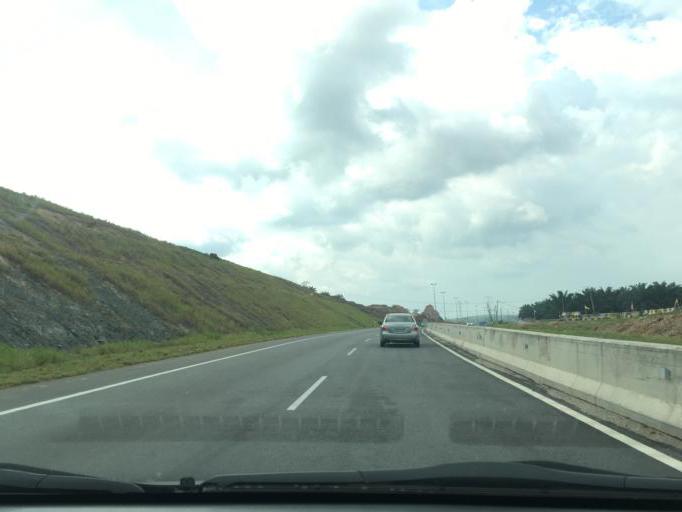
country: MY
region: Selangor
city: Batu Arang
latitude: 3.2891
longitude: 101.4418
